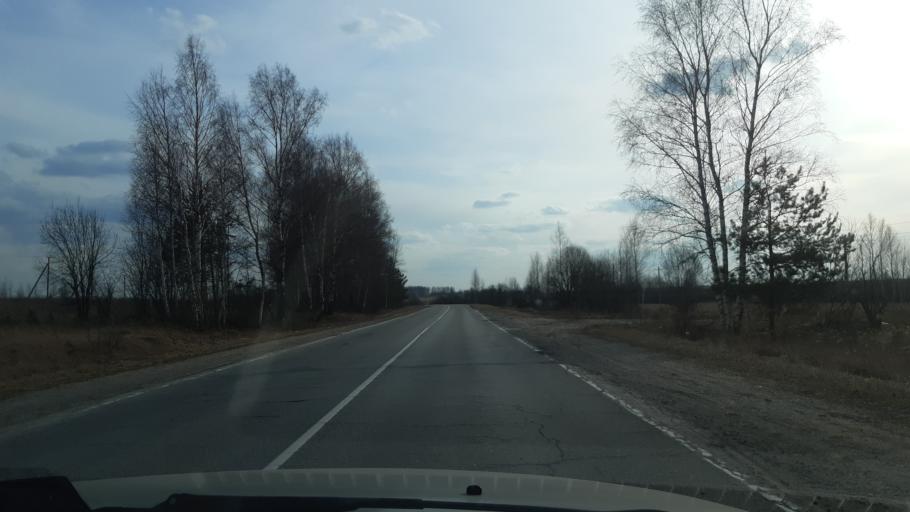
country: RU
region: Vladimir
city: Nikologory
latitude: 56.1743
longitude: 42.0031
